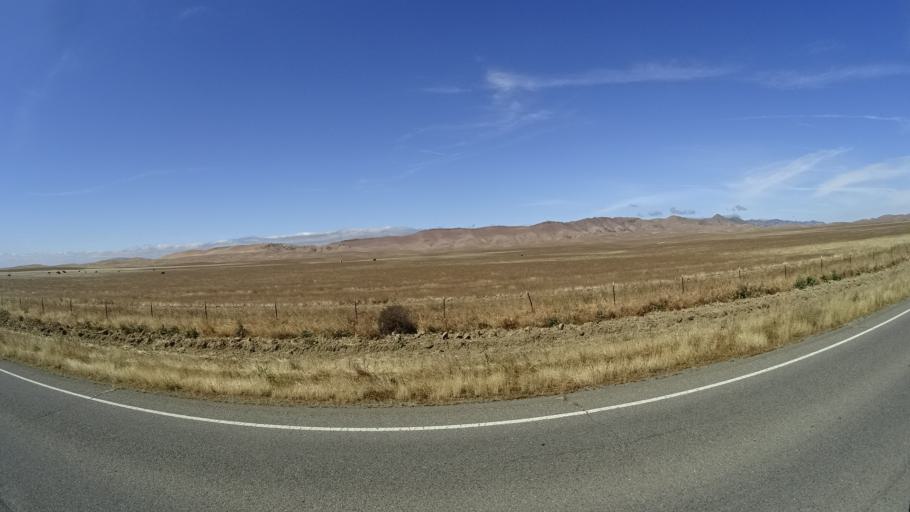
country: US
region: California
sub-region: Kings County
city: Avenal
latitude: 35.9329
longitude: -120.0833
